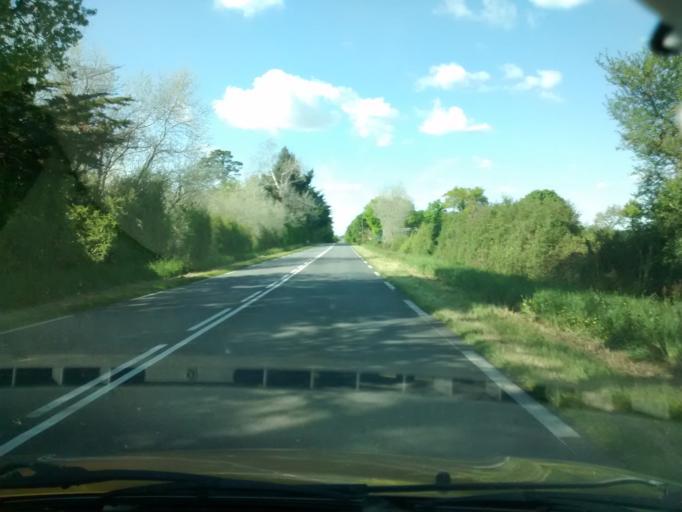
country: FR
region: Pays de la Loire
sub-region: Departement de la Vendee
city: Rocheserviere
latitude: 46.8982
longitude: -1.5024
